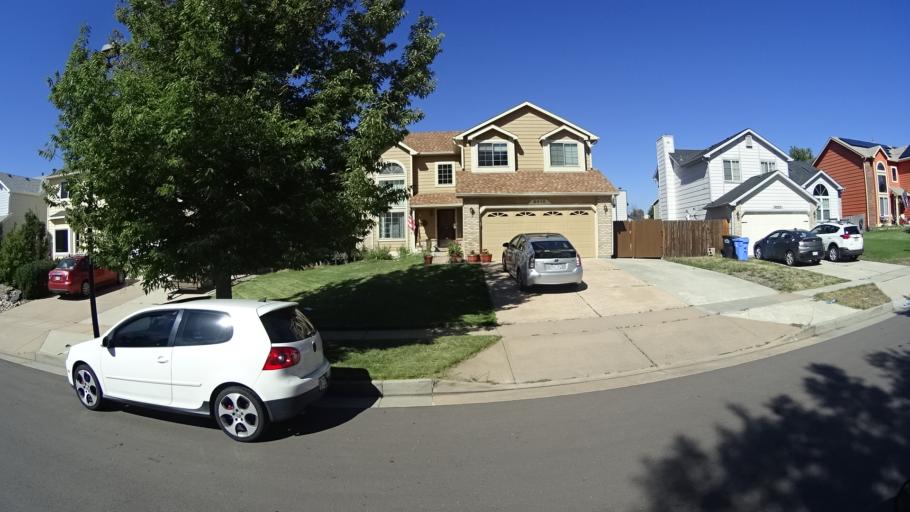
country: US
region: Colorado
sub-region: El Paso County
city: Black Forest
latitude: 38.9480
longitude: -104.7387
